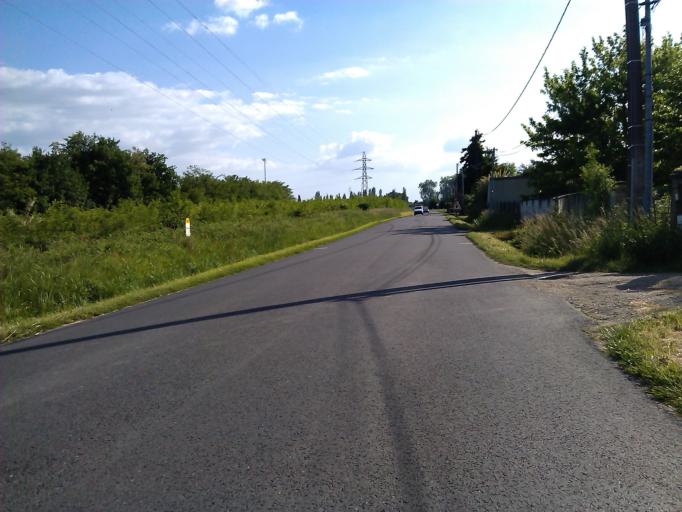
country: FR
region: Aquitaine
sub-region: Departement de la Gironde
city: Saint-Gervais
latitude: 45.0137
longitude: -0.4456
